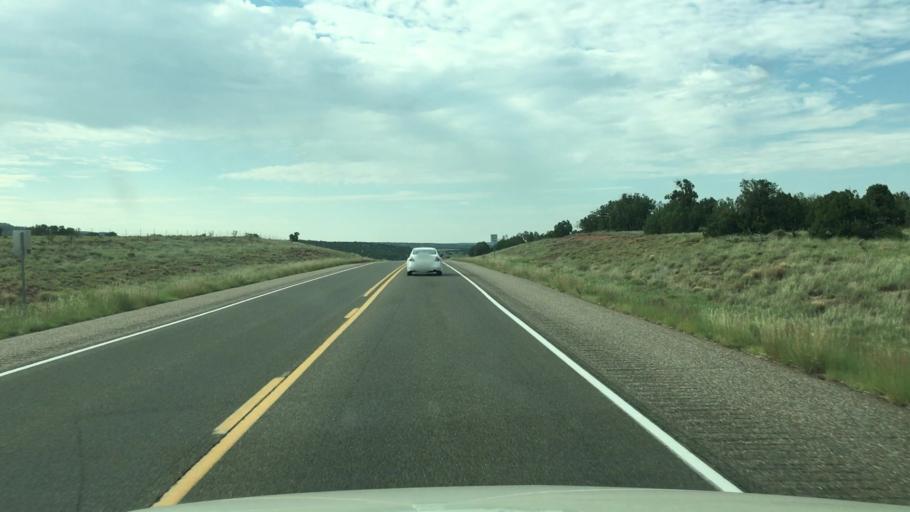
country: US
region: New Mexico
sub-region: Santa Fe County
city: Eldorado at Santa Fe
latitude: 35.3127
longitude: -105.8301
